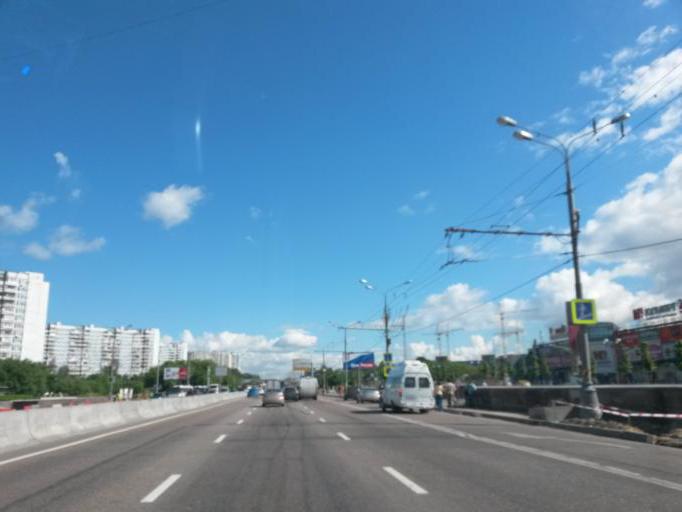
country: RU
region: Moscow
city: Annino
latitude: 55.5832
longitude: 37.5975
